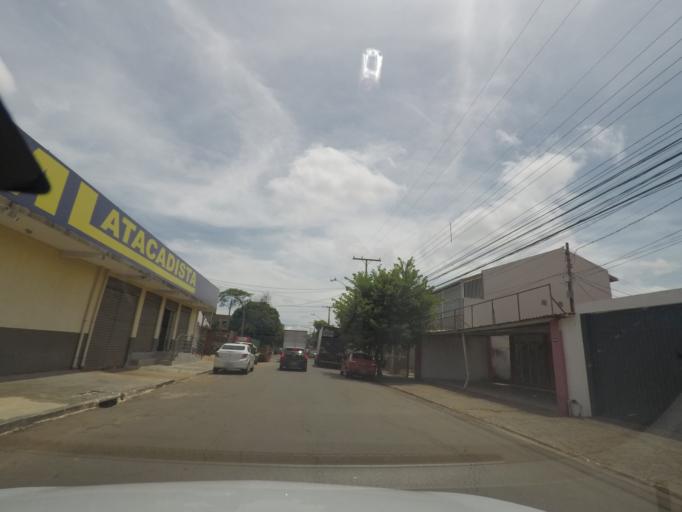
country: BR
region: Goias
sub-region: Goiania
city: Goiania
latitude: -16.6898
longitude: -49.3081
